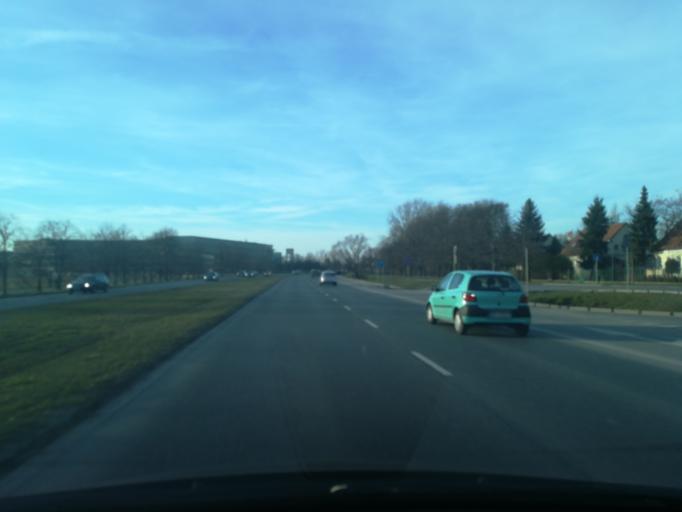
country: PL
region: Masovian Voivodeship
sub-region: Warszawa
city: Wilanow
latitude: 52.1613
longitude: 21.0857
